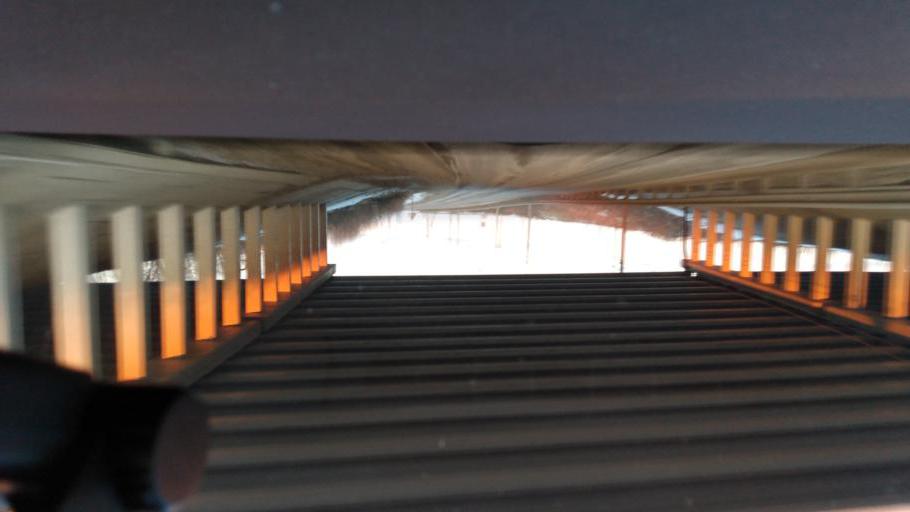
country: RU
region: Moskovskaya
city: Kolomna
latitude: 55.0890
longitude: 38.9050
